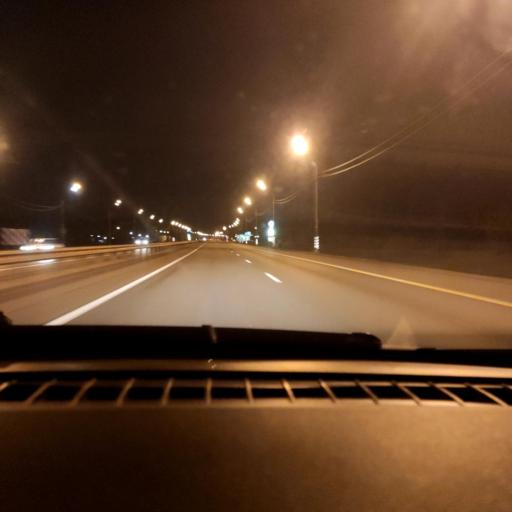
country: RU
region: Lipetsk
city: Khlevnoye
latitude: 52.2657
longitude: 39.0599
